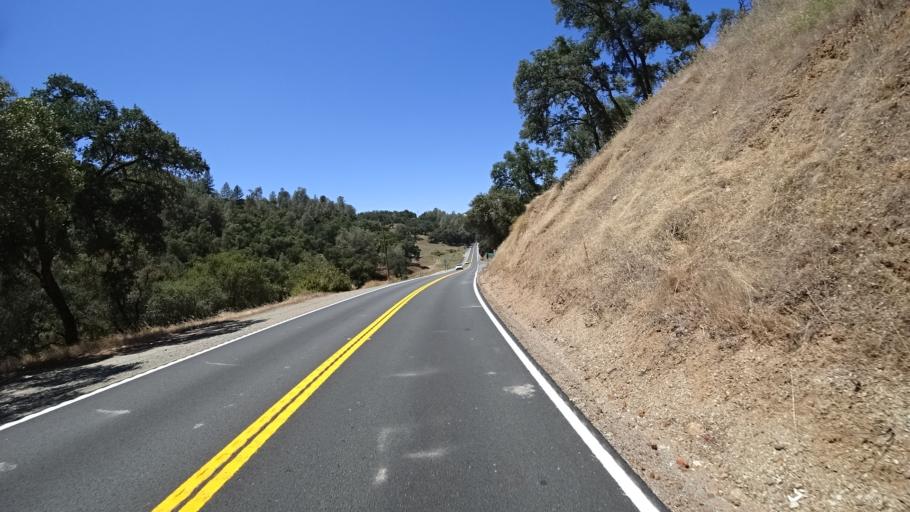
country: US
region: California
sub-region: Calaveras County
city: San Andreas
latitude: 38.2011
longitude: -120.7217
